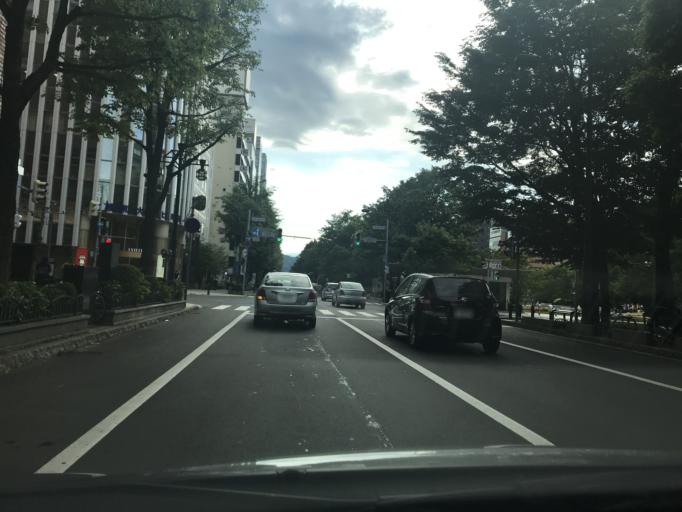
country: JP
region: Hokkaido
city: Sapporo
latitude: 43.0600
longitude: 141.3512
